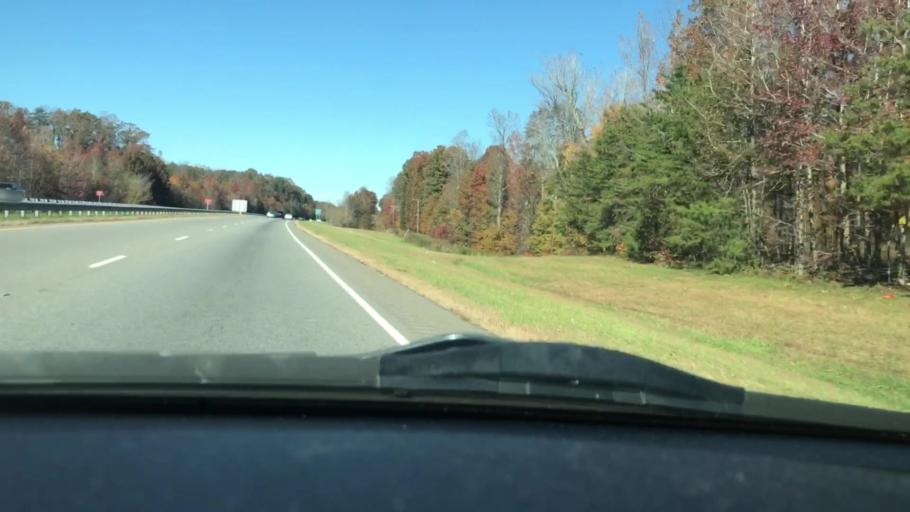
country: US
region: North Carolina
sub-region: Rockingham County
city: Madison
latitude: 36.3916
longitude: -79.9410
